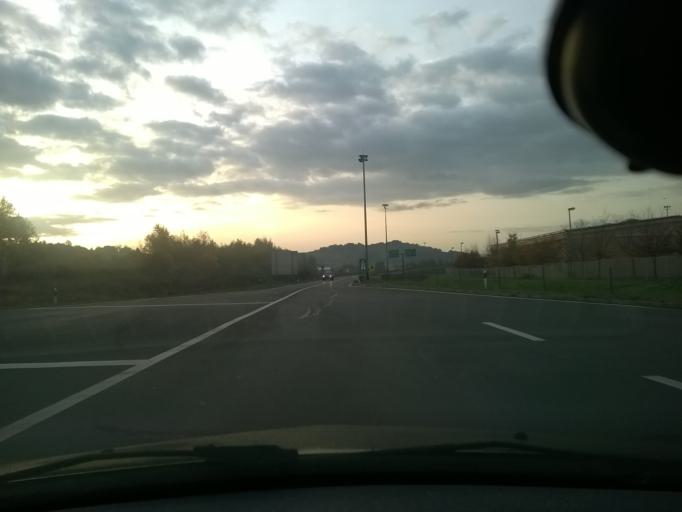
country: HR
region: Krapinsko-Zagorska
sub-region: Grad Krapina
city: Krapina
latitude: 46.1329
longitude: 15.8837
